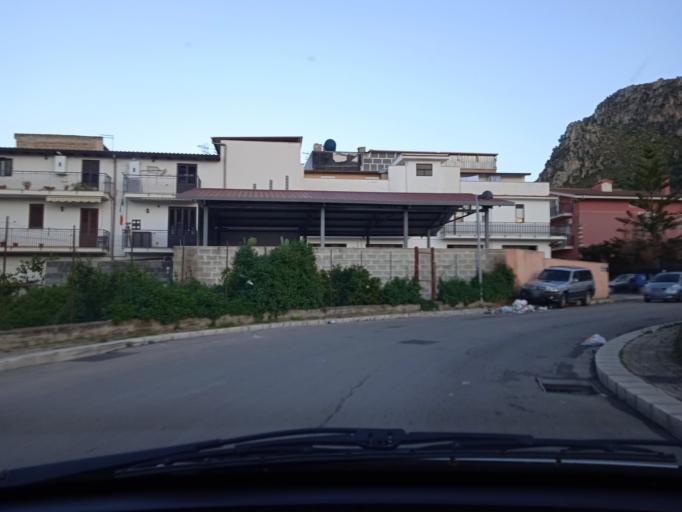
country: IT
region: Sicily
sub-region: Palermo
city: Villabate
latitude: 38.0748
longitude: 13.4433
